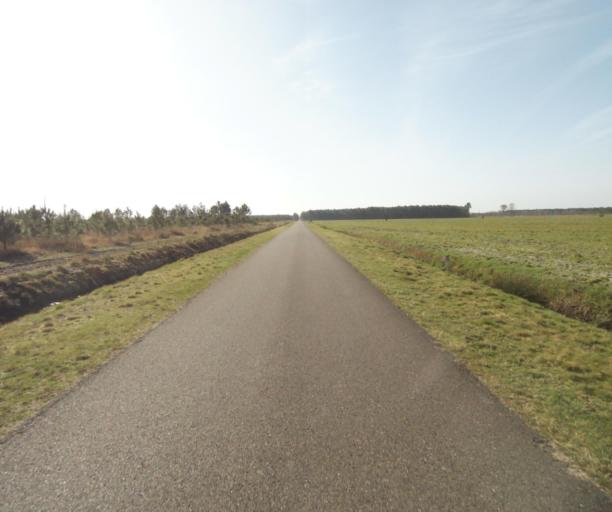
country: FR
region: Aquitaine
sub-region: Departement de la Gironde
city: Grignols
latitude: 44.1936
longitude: -0.1432
